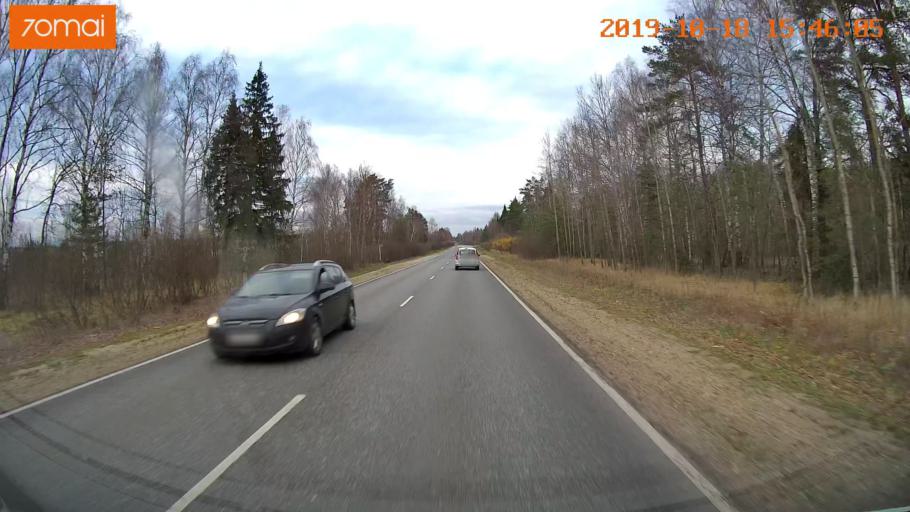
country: RU
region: Vladimir
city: Golovino
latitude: 56.0025
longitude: 40.5666
